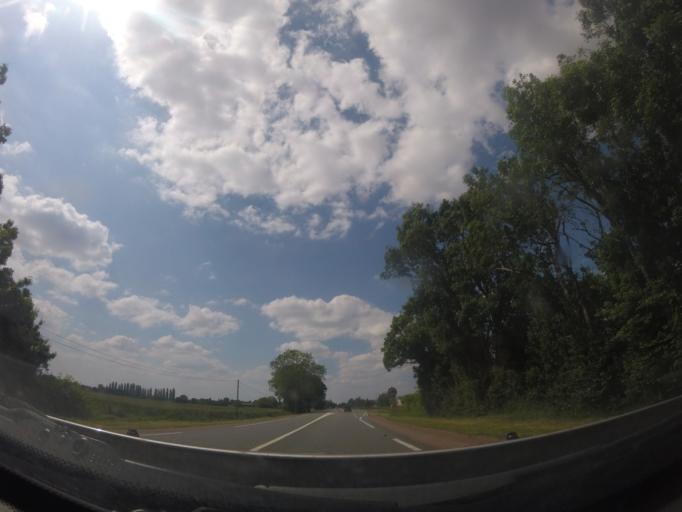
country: FR
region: Poitou-Charentes
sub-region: Departement de la Charente-Maritime
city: Bords
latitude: 45.8529
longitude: -0.8260
